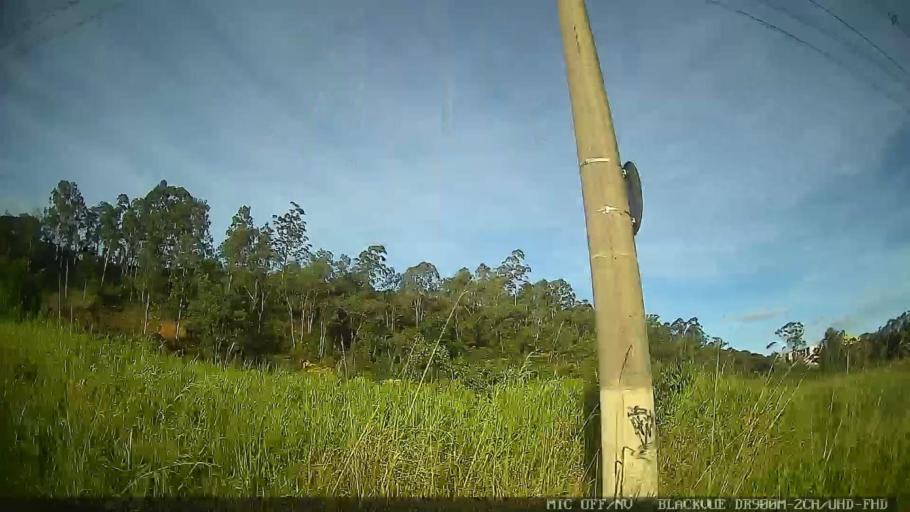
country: BR
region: Sao Paulo
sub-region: Mogi das Cruzes
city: Mogi das Cruzes
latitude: -23.5197
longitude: -46.1489
